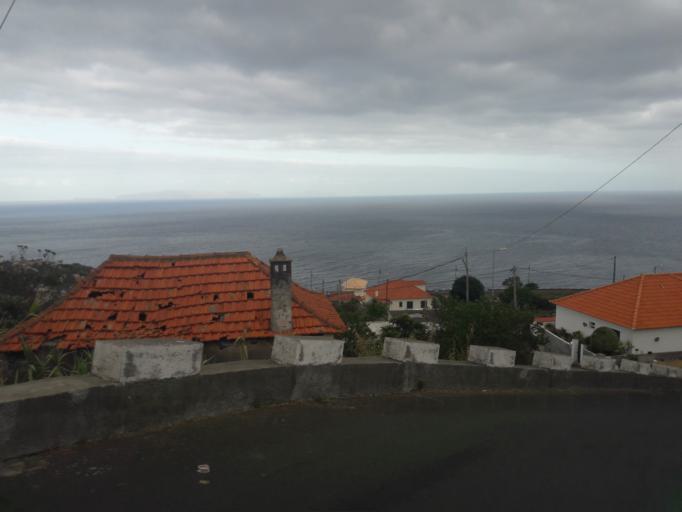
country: PT
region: Madeira
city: Canico
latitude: 32.6431
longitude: -16.8428
